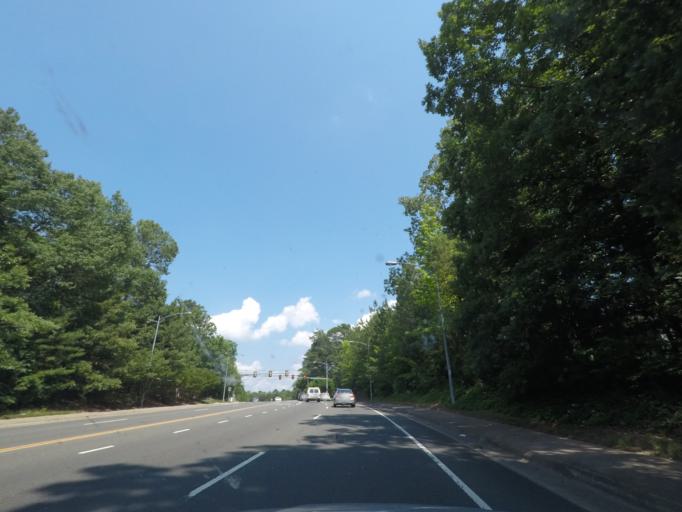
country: US
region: North Carolina
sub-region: Durham County
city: Durham
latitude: 35.9586
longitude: -78.9487
